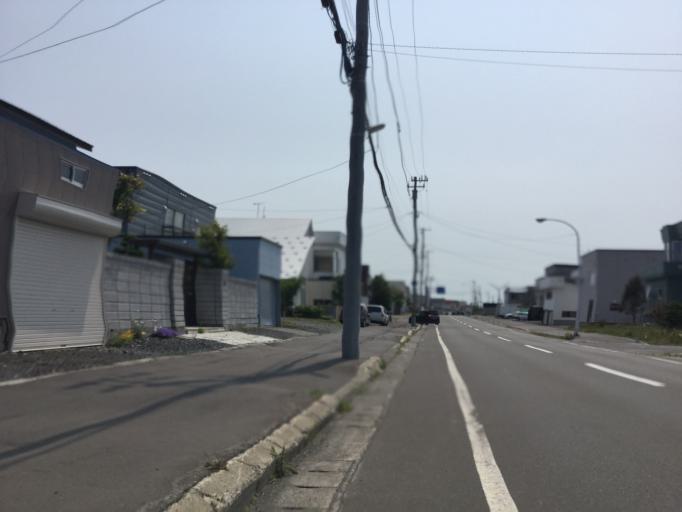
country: JP
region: Hokkaido
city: Wakkanai
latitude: 45.3869
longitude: 141.7223
